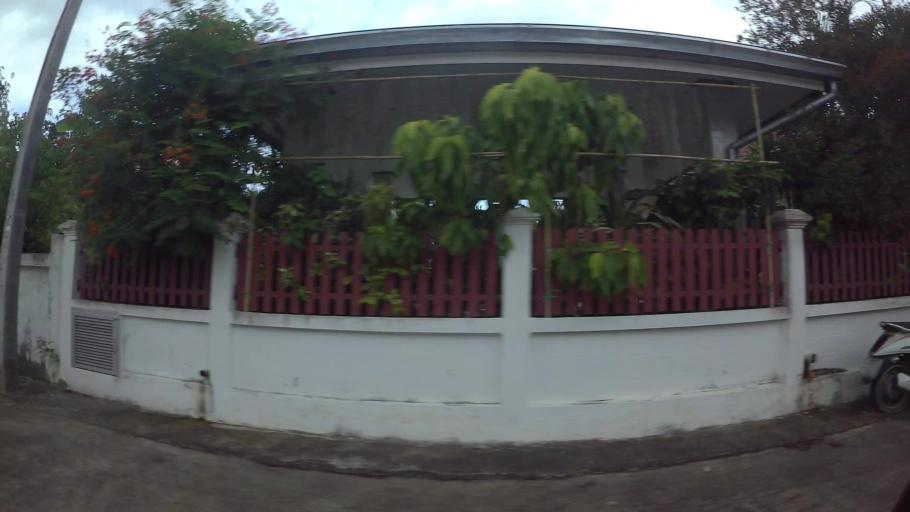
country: TH
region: Chon Buri
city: Sattahip
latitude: 12.7243
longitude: 100.9063
